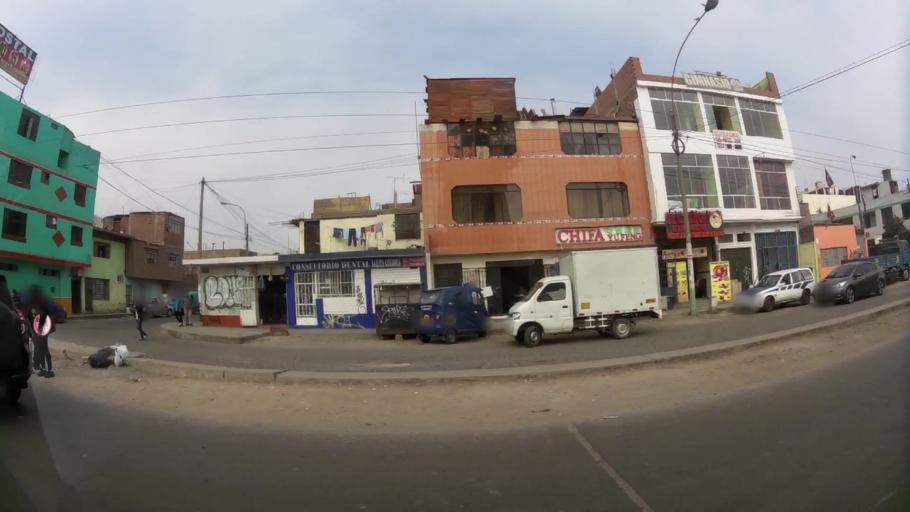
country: PE
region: Callao
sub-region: Callao
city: Callao
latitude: -12.0339
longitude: -77.0962
